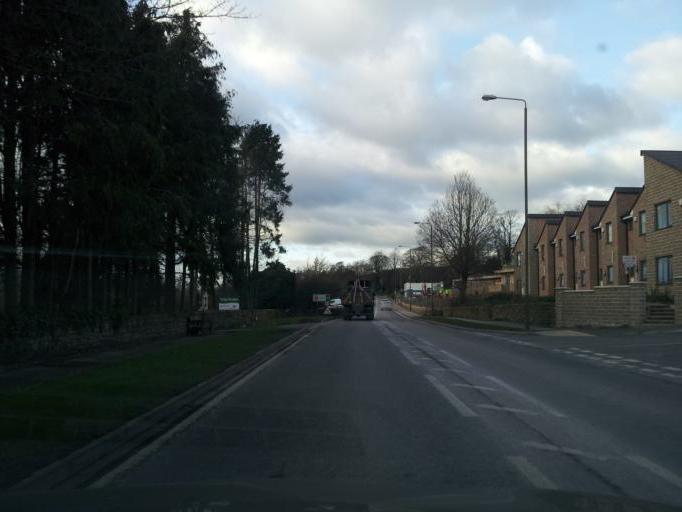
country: GB
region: England
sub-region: Derbyshire
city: Matlock
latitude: 53.1486
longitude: -1.5741
